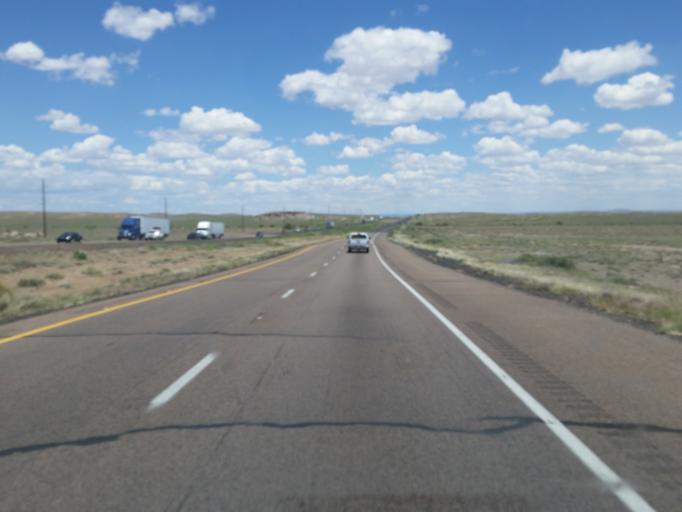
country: US
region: Arizona
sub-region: Navajo County
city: Holbrook
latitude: 34.9911
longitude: -109.9911
